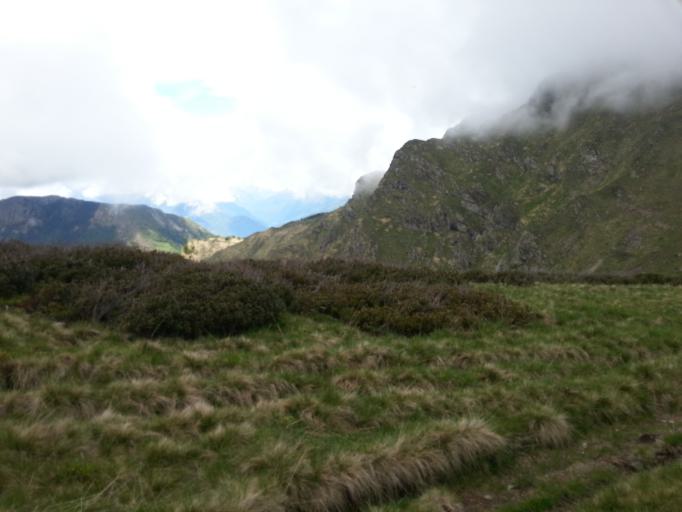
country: CH
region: Ticino
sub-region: Locarno District
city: Magadino
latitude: 46.0960
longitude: 8.8665
